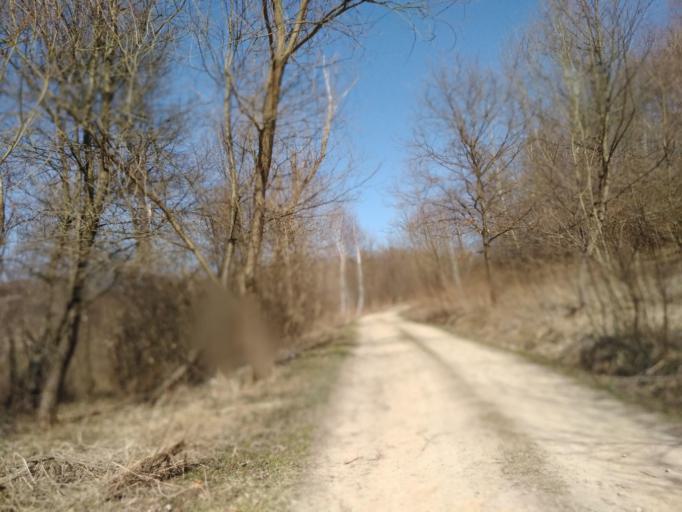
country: PL
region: Subcarpathian Voivodeship
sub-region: Powiat brzozowski
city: Blizne
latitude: 49.7243
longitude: 21.9736
